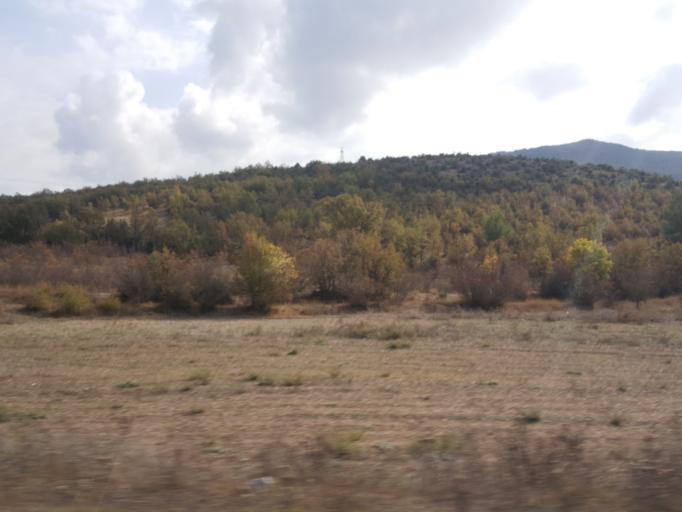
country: TR
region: Sinop
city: Sarayduzu
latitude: 41.3720
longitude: 34.8989
